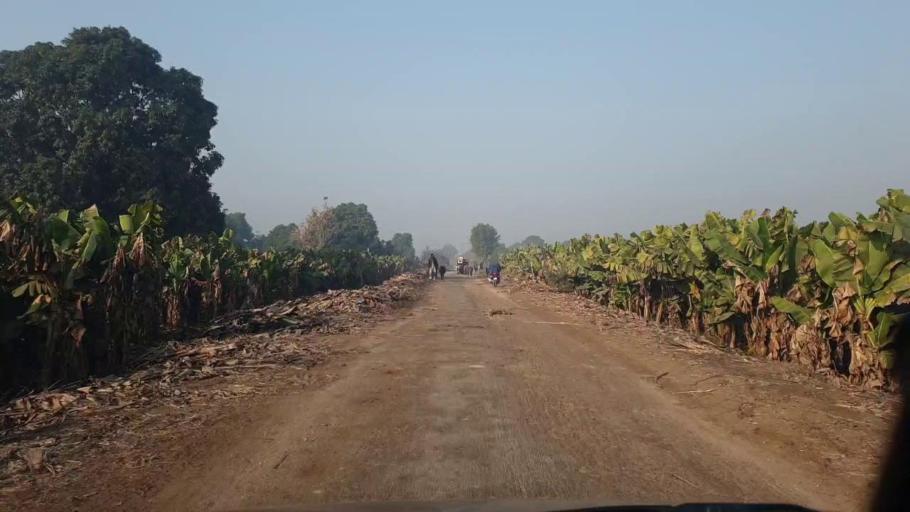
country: PK
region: Sindh
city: Shahdadpur
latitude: 25.8507
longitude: 68.6454
